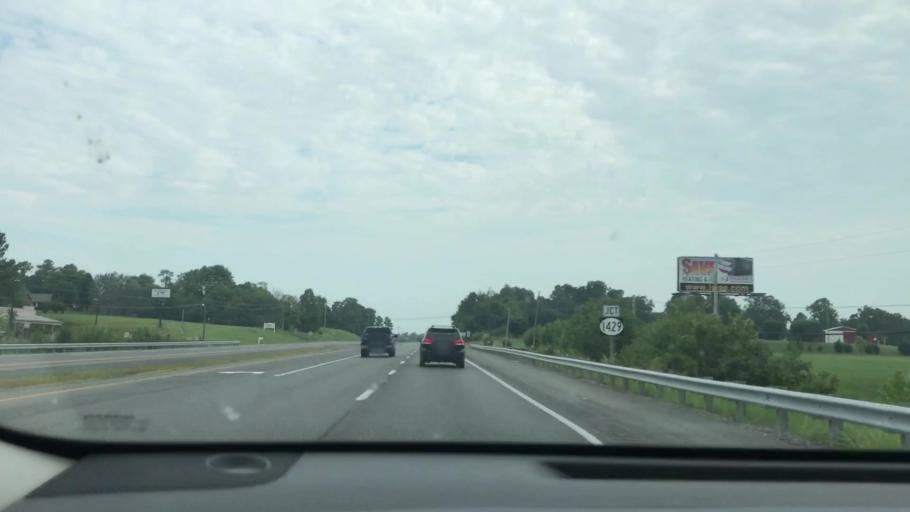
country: US
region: Kentucky
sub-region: Calloway County
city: Murray
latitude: 36.6663
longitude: -88.3043
